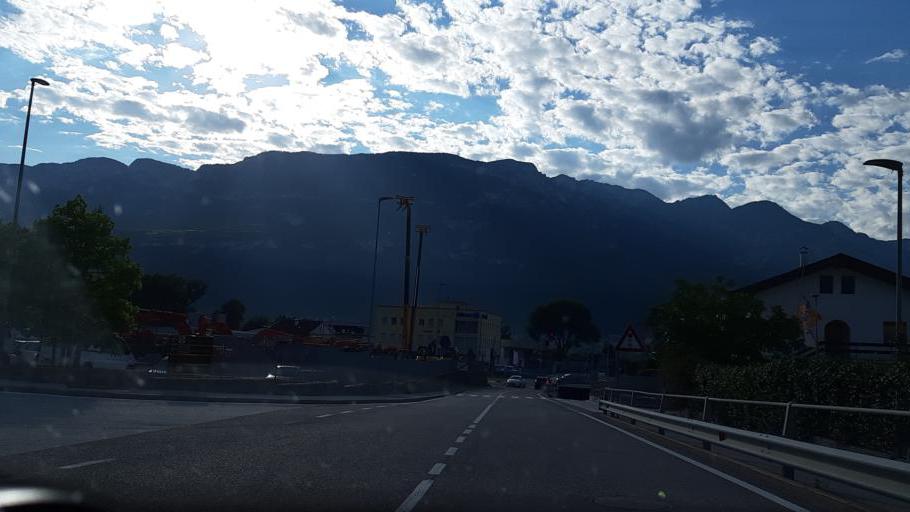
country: IT
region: Trentino-Alto Adige
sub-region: Bolzano
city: Egna
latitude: 46.3226
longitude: 11.2751
